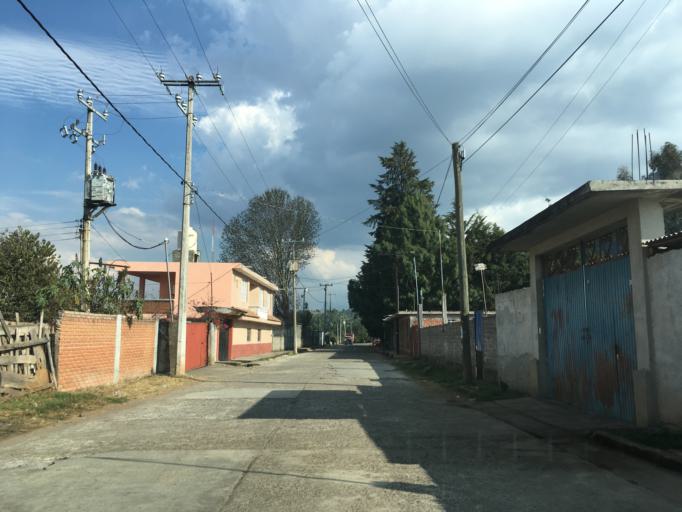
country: MX
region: Michoacan
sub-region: Patzcuaro
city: Santa Ana Chapitiro
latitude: 19.5254
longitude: -101.6504
